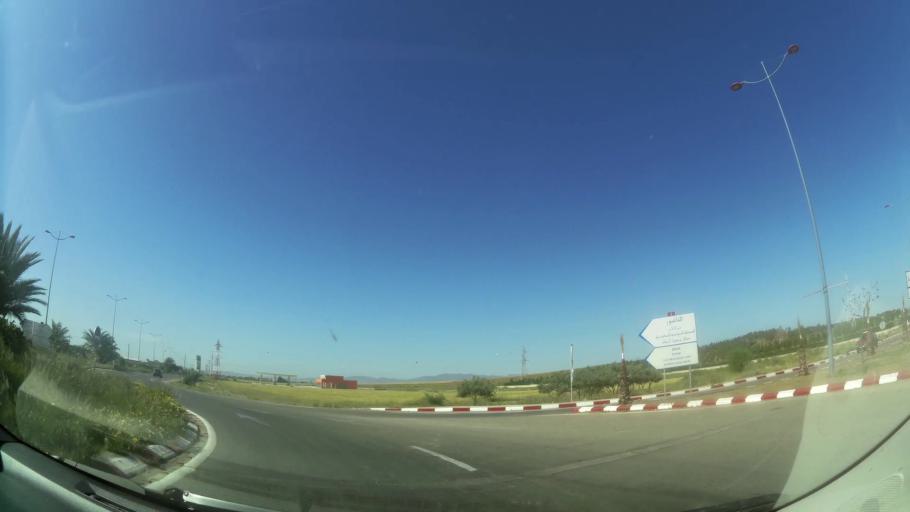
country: MA
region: Oriental
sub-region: Oujda-Angad
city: Oujda
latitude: 34.7375
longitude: -1.9291
